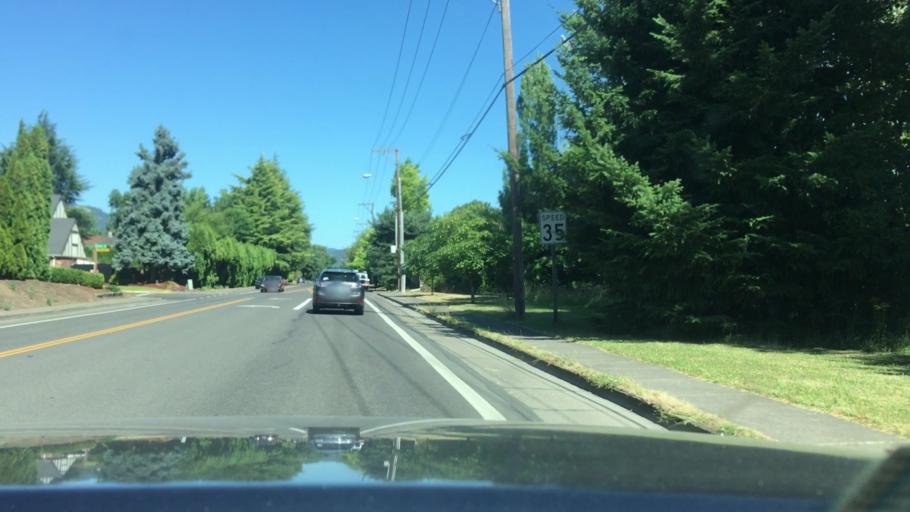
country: US
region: Oregon
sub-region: Lane County
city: Eugene
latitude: 44.0929
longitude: -123.0789
